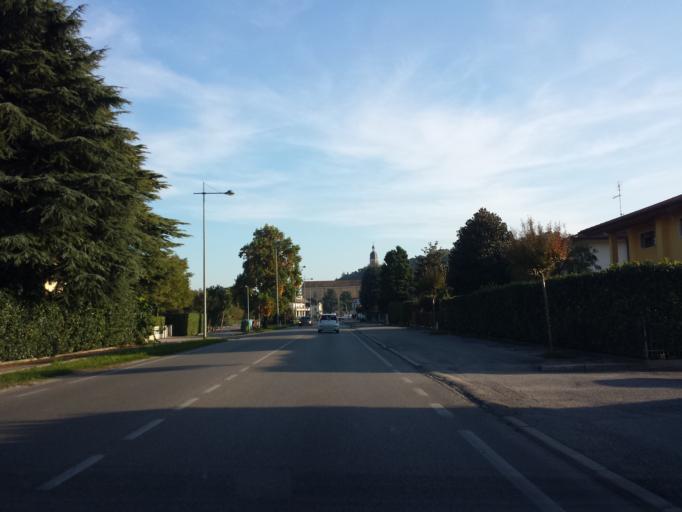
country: IT
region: Veneto
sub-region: Provincia di Vicenza
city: Isola Vicentina
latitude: 45.6333
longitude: 11.4392
